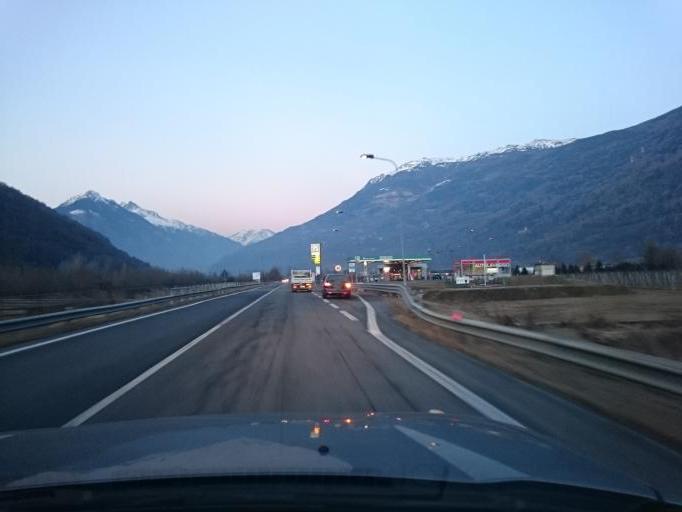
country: IT
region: Lombardy
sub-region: Provincia di Sondrio
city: Lovero
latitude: 46.2371
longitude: 10.2294
